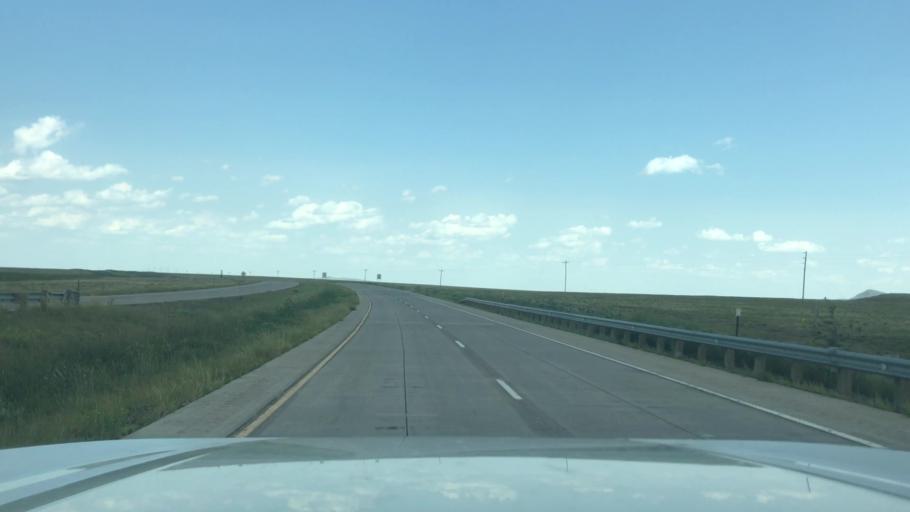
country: US
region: New Mexico
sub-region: Union County
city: Clayton
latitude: 36.6147
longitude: -103.6851
